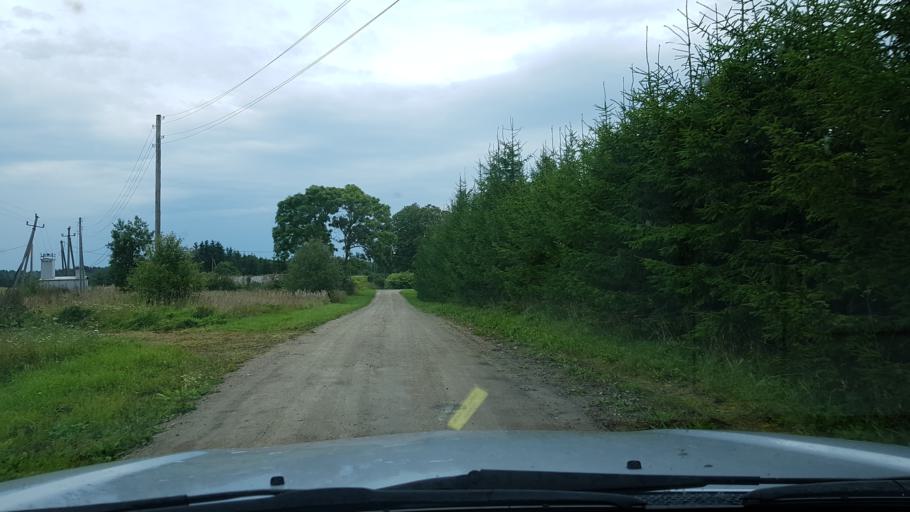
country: EE
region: Harju
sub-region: Rae vald
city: Jueri
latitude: 59.3392
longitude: 24.9443
